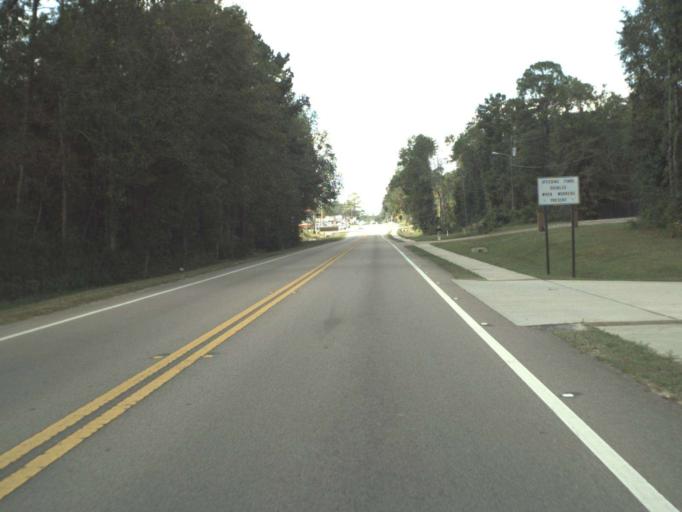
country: US
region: Florida
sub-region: Walton County
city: Freeport
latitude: 30.4948
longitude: -86.1291
